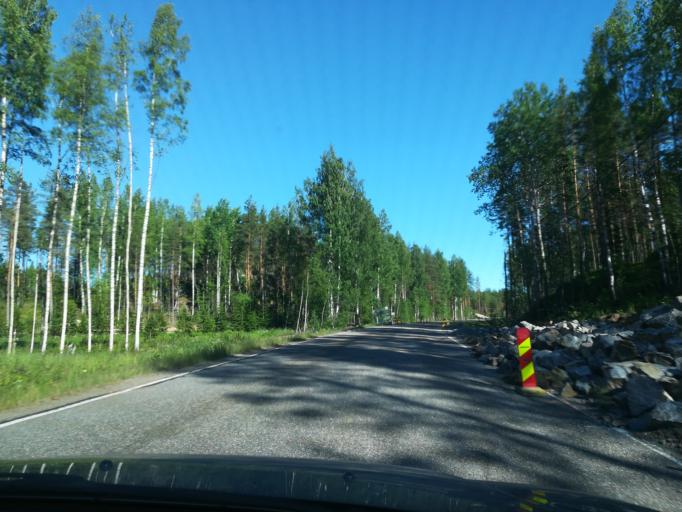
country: FI
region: Southern Savonia
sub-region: Mikkeli
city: Puumala
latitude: 61.4673
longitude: 28.3248
